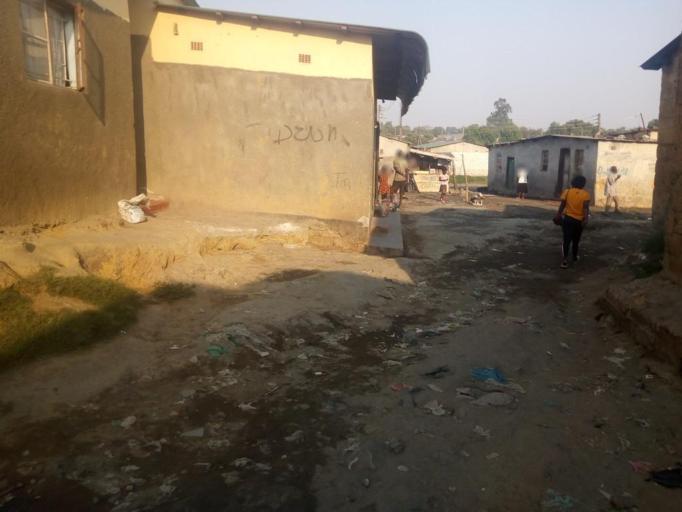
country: ZM
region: Lusaka
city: Lusaka
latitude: -15.4044
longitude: 28.3632
